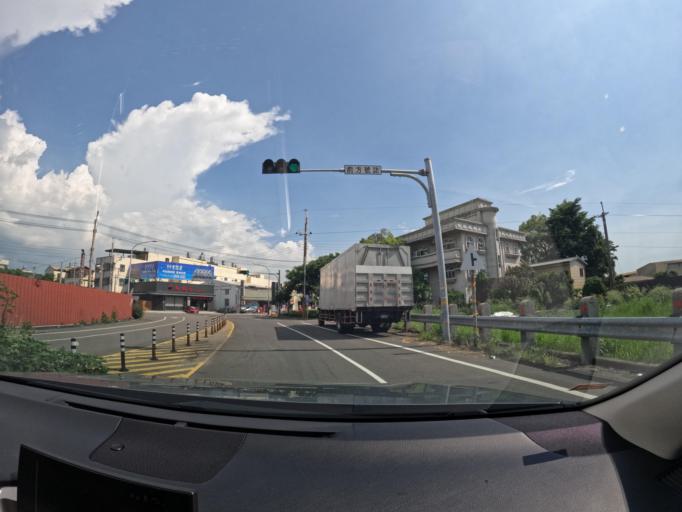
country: TW
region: Taiwan
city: Fengyuan
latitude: 24.3120
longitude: 120.7183
